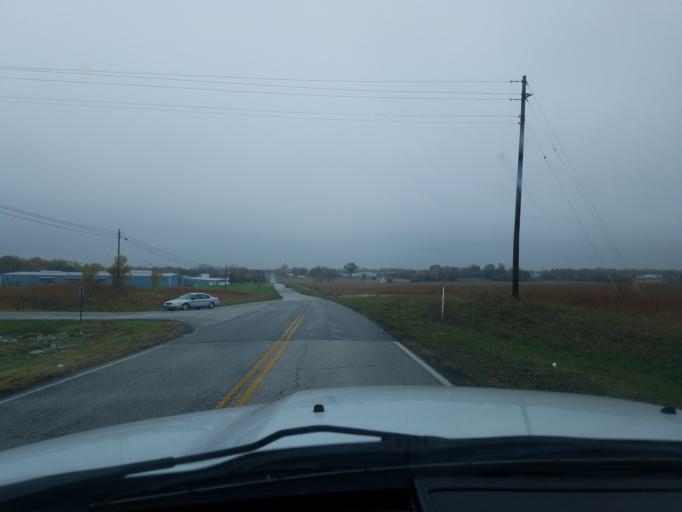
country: US
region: Kentucky
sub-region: Taylor County
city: Campbellsville
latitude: 37.3439
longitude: -85.3245
